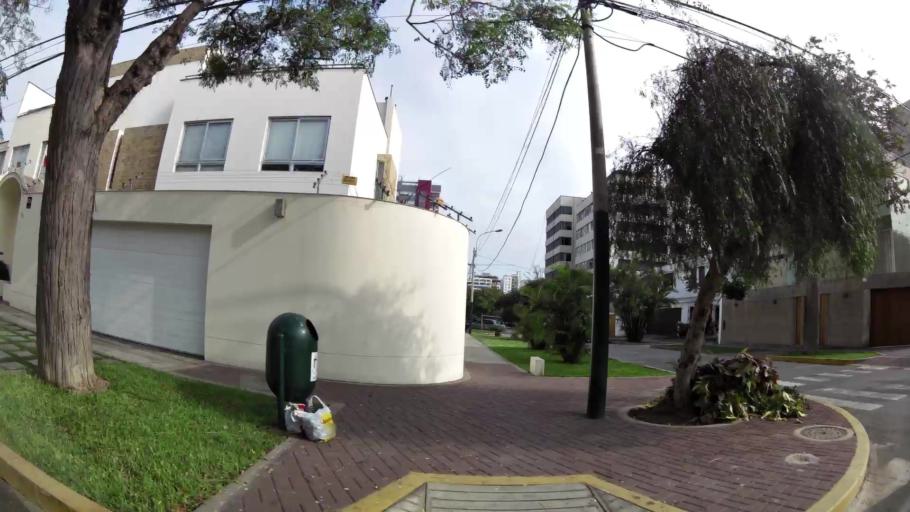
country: PE
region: Lima
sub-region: Lima
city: San Isidro
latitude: -12.0934
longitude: -77.0558
